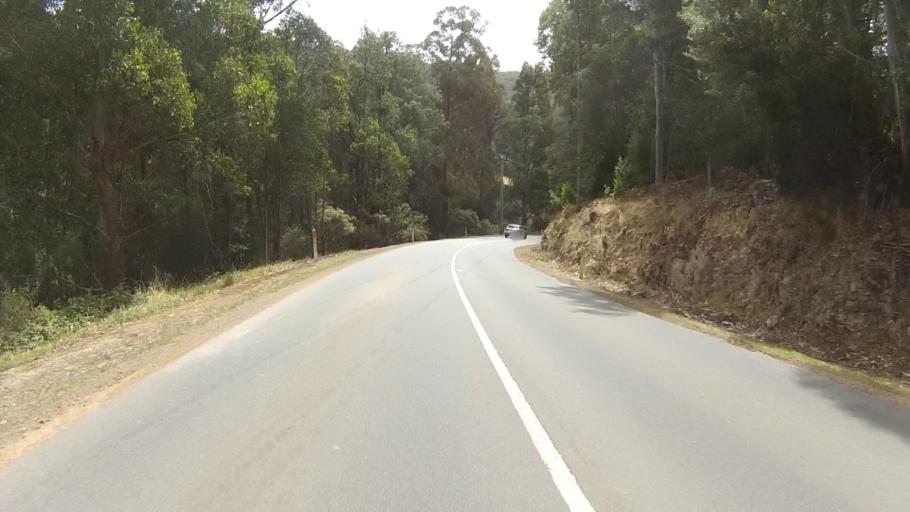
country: AU
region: Tasmania
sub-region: Kingborough
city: Kettering
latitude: -43.1080
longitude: 147.2023
